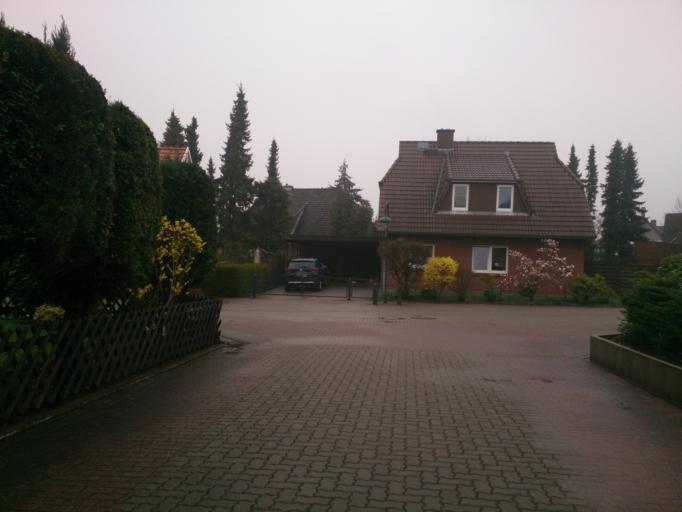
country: DE
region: Lower Saxony
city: Neu Wulmstorf
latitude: 53.4689
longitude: 9.7964
